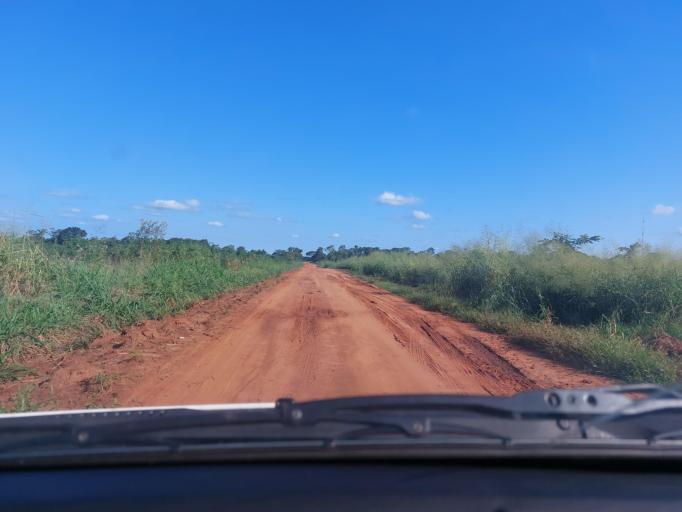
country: PY
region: San Pedro
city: Guayaybi
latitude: -24.5260
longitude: -56.5454
